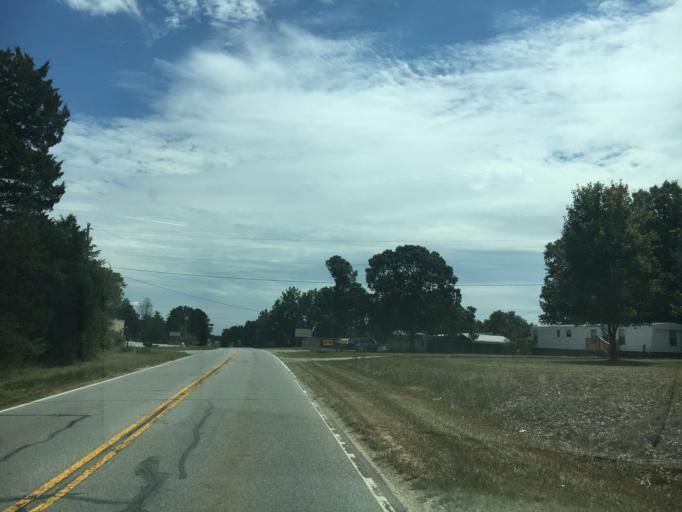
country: US
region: South Carolina
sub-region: Laurens County
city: Laurens
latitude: 34.5810
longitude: -82.0971
